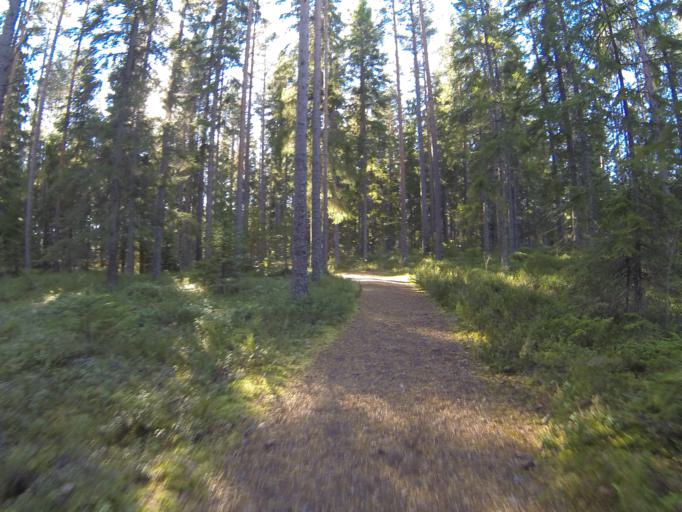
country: FI
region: Varsinais-Suomi
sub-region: Salo
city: Saerkisalo
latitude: 60.2078
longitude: 22.9401
